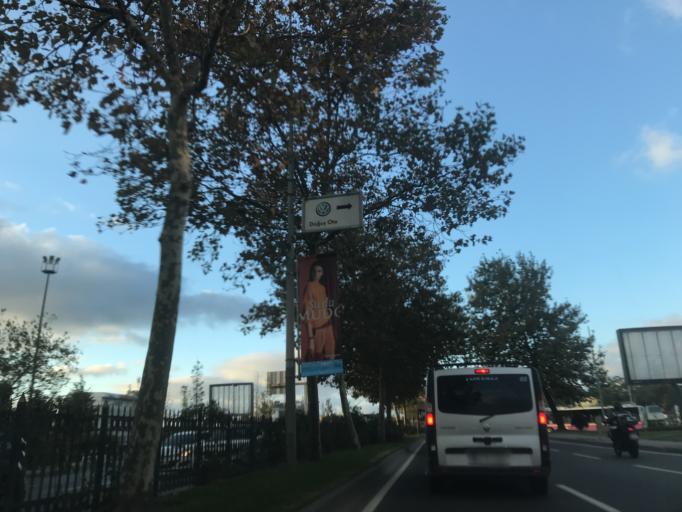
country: TR
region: Istanbul
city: Sisli
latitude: 41.1144
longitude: 29.0247
